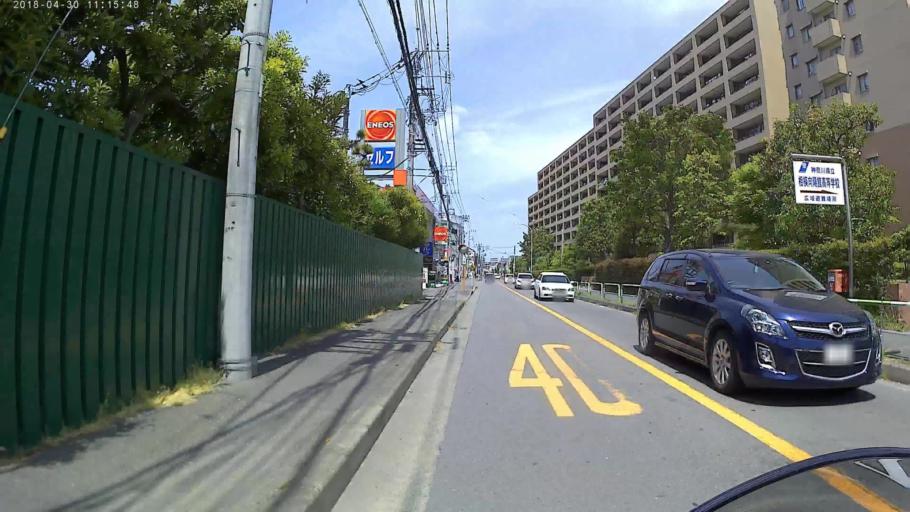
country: JP
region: Kanagawa
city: Minami-rinkan
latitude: 35.4789
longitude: 139.4341
